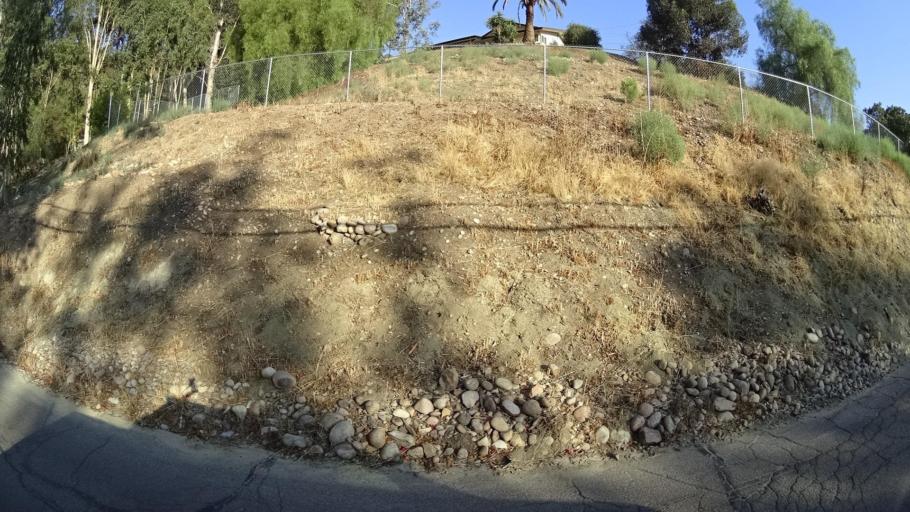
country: US
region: California
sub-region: San Diego County
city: Eucalyptus Hills
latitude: 32.8947
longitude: -116.9485
